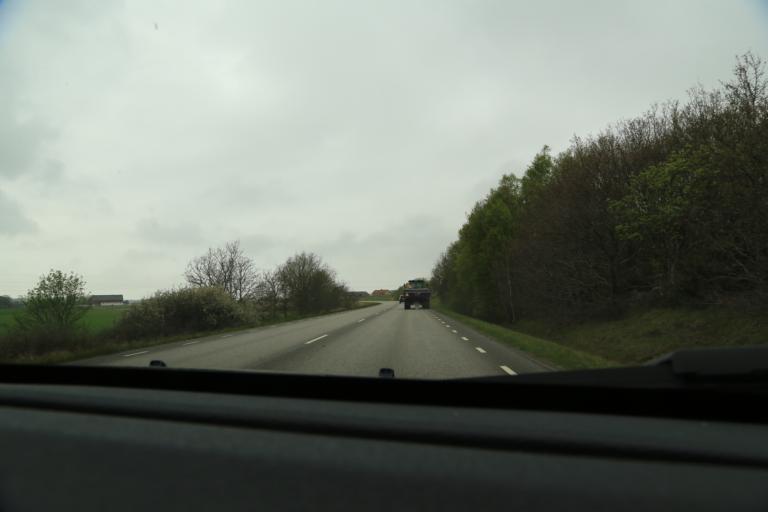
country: SE
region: Halland
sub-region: Kungsbacka Kommun
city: Frillesas
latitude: 57.2377
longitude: 12.1765
